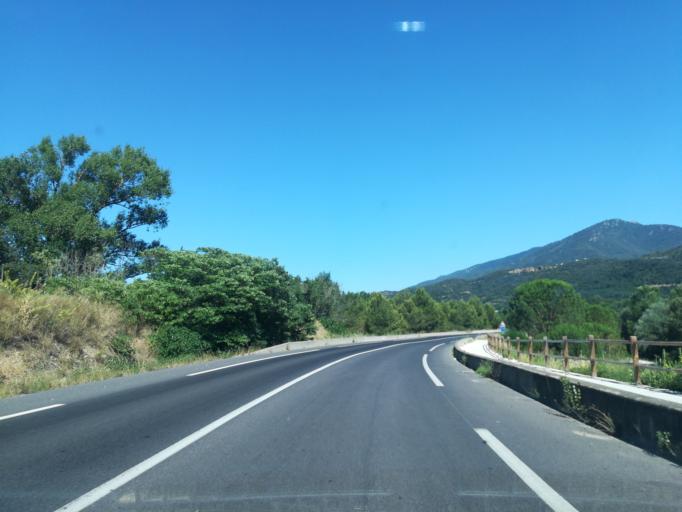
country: FR
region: Languedoc-Roussillon
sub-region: Departement des Pyrenees-Orientales
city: el Volo
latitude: 42.5200
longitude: 2.8253
